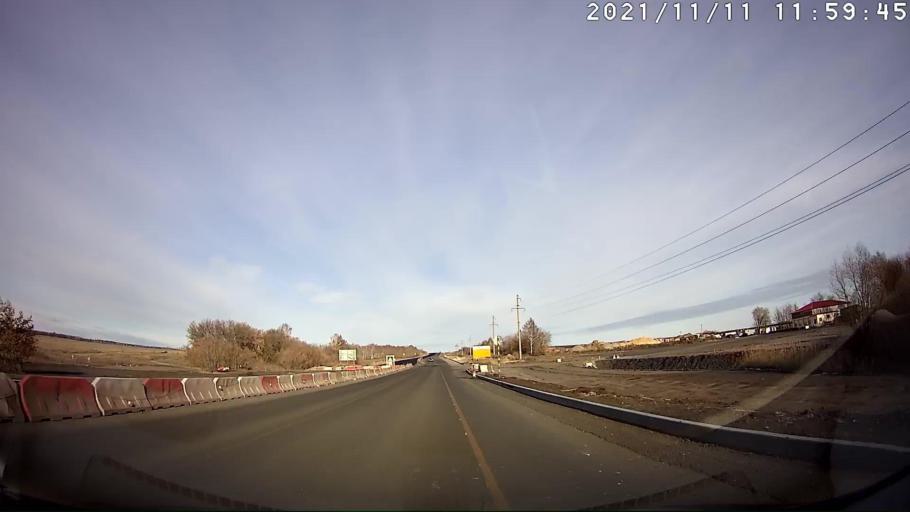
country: RU
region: Ulyanovsk
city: Silikatnyy
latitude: 53.5965
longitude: 48.3370
